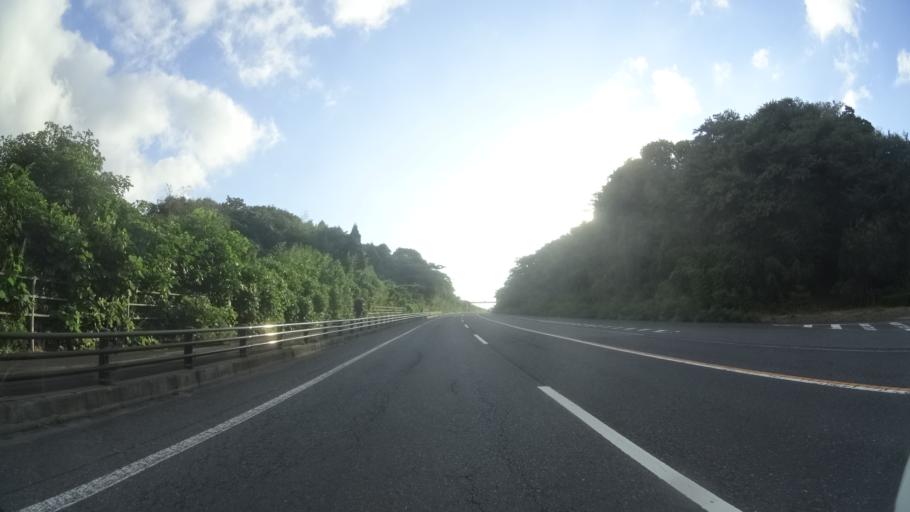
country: JP
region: Tottori
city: Yonago
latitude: 35.5165
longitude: 133.5504
